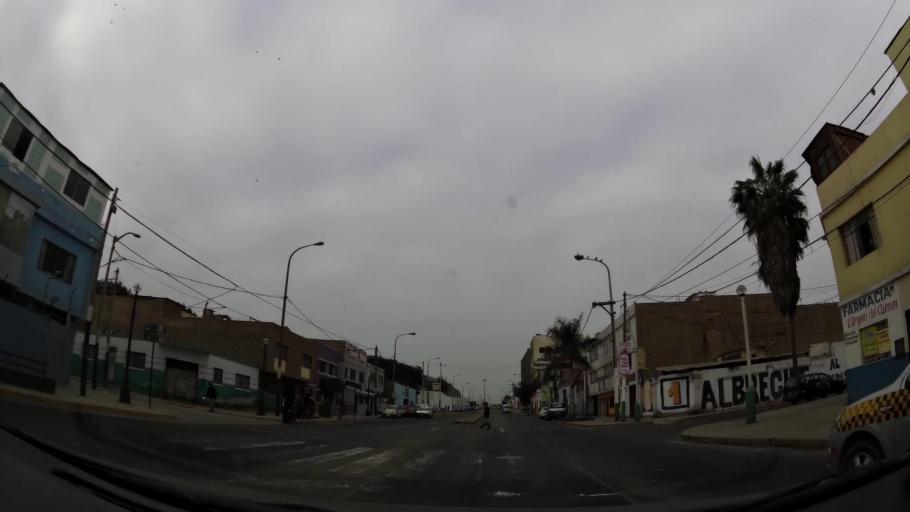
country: PE
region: Callao
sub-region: Callao
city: Callao
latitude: -12.0663
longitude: -77.1242
